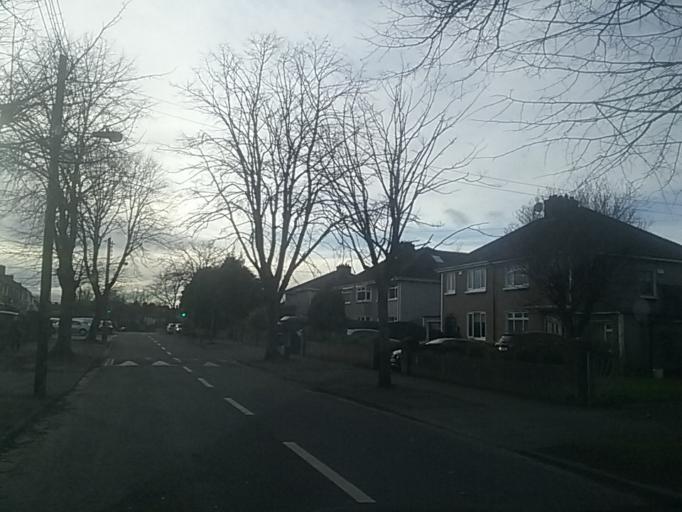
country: IE
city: Coolock
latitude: 53.3788
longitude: -6.1929
